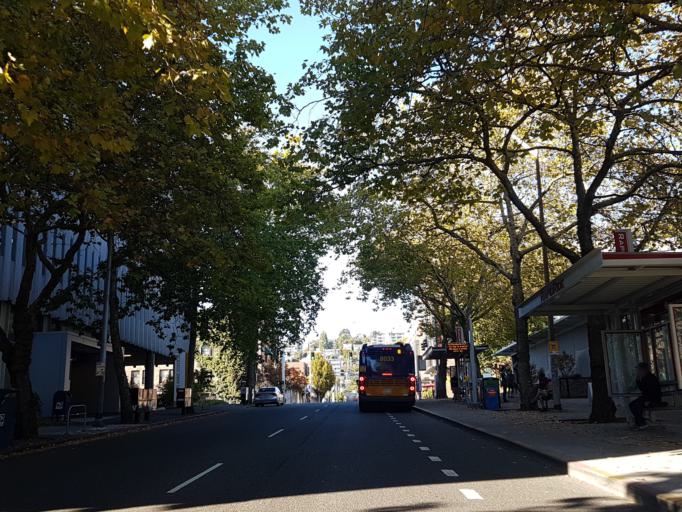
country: US
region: Washington
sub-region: King County
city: Seattle
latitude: 47.6226
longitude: -122.3553
